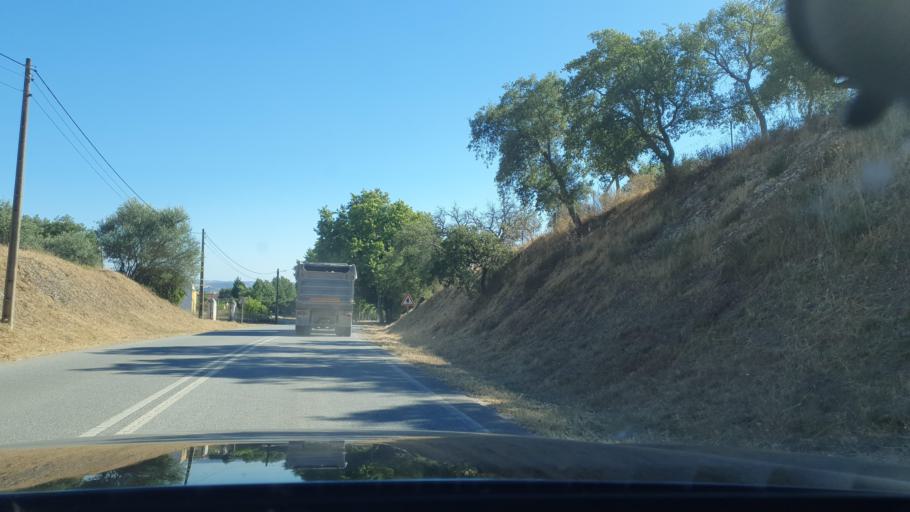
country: PT
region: Evora
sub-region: Alandroal
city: Alandroal
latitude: 38.7073
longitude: -7.4063
